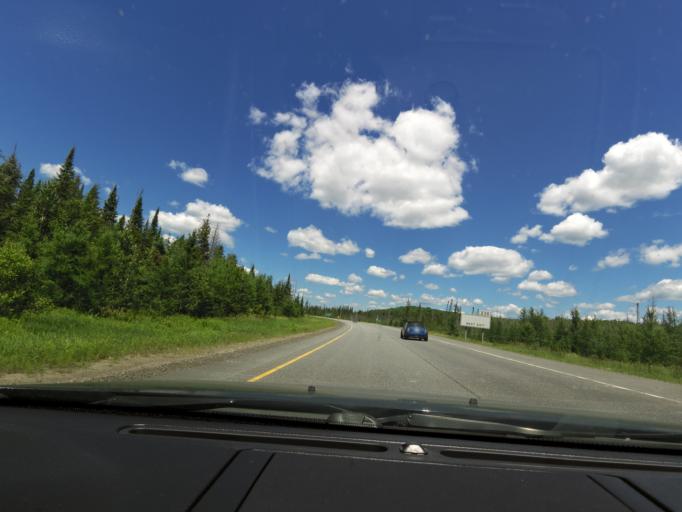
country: CA
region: Ontario
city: Huntsville
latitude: 45.4300
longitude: -79.2385
